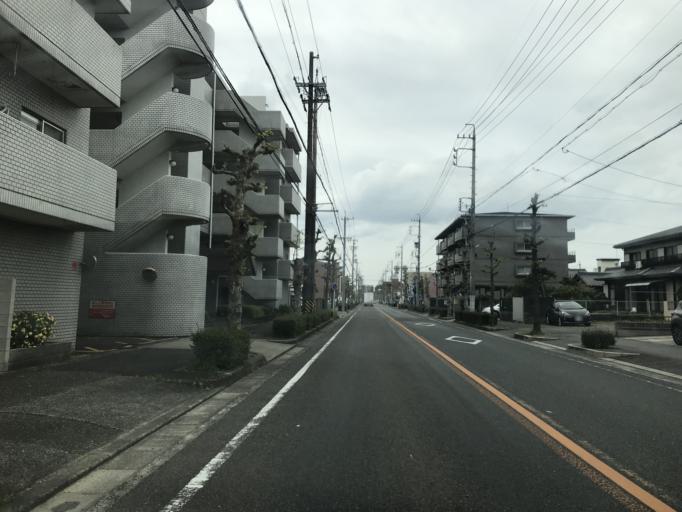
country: JP
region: Aichi
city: Kasugai
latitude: 35.2420
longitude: 136.9785
